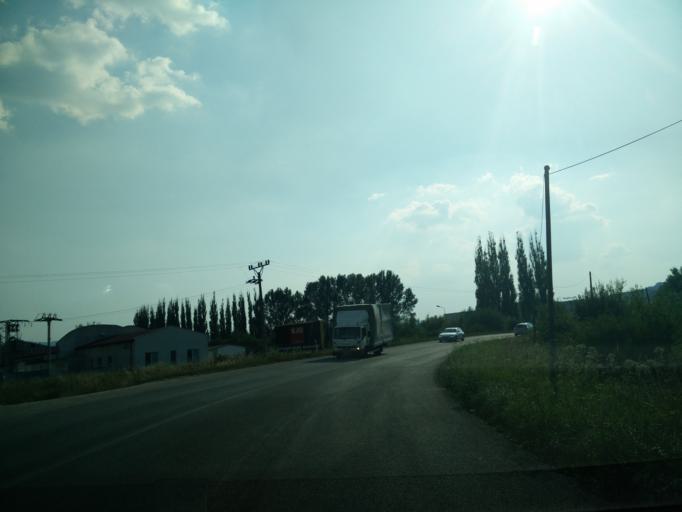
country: SK
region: Zilinsky
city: Rajec
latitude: 49.0956
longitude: 18.6439
